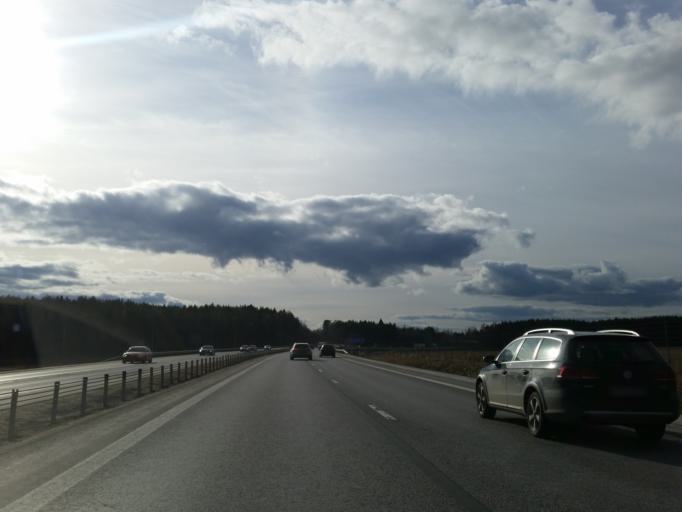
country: SE
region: Soedermanland
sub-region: Nykopings Kommun
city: Nykoping
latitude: 58.7458
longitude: 16.9466
